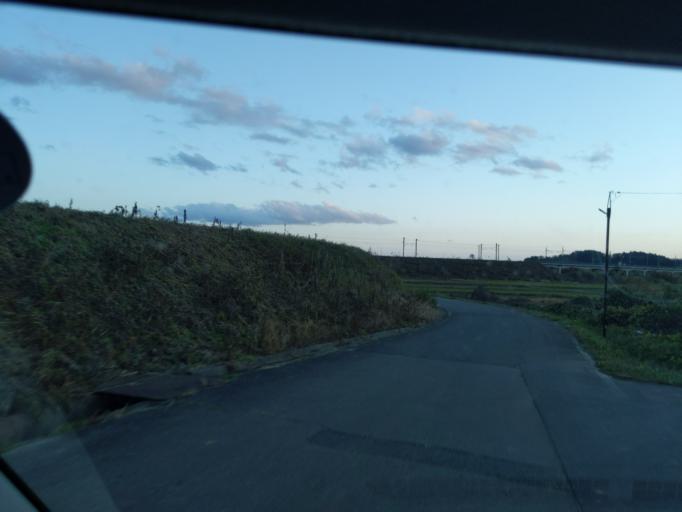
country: JP
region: Iwate
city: Ichinoseki
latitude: 39.0109
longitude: 141.1131
